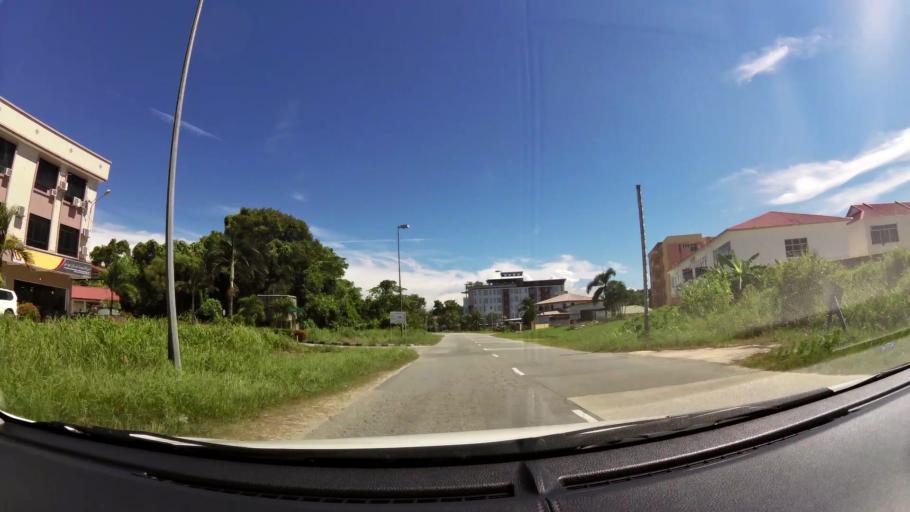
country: BN
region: Brunei and Muara
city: Bandar Seri Begawan
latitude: 5.0273
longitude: 115.0622
